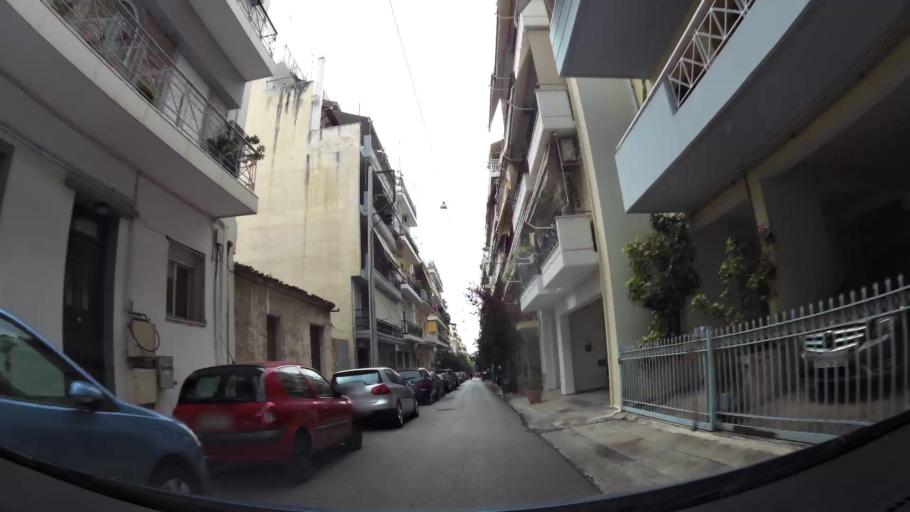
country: GR
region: Attica
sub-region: Nomarchia Athinas
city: Kaisariani
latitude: 37.9669
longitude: 23.7613
